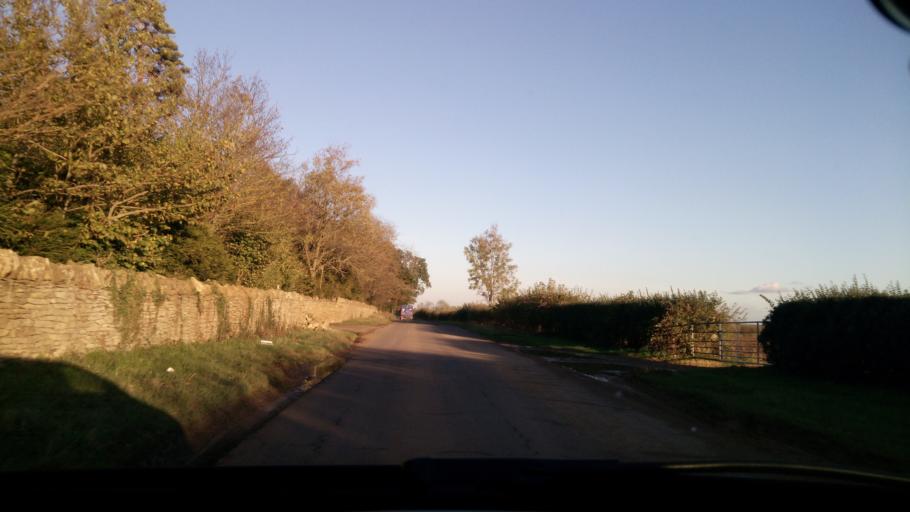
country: GB
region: England
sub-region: Peterborough
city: Wittering
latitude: 52.6251
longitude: -0.4472
